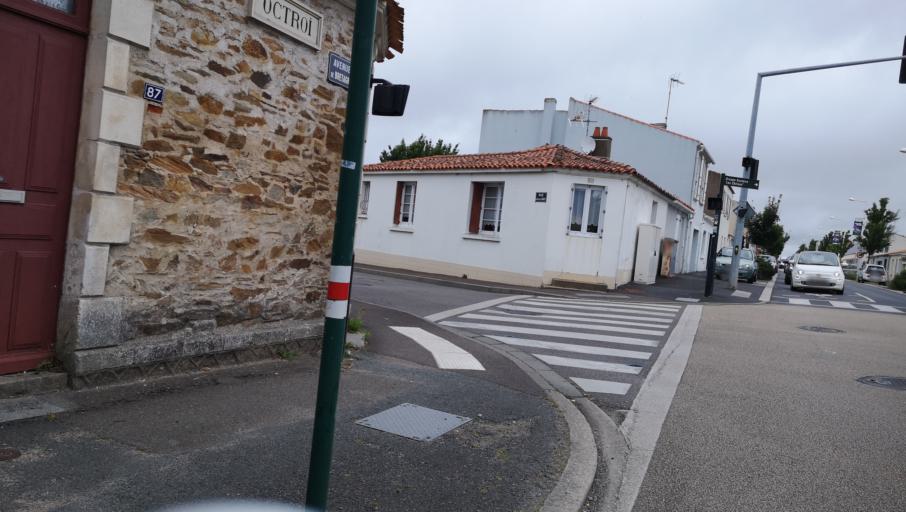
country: FR
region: Pays de la Loire
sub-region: Departement de la Vendee
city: Les Sables-d'Olonne
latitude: 46.5069
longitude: -1.7774
